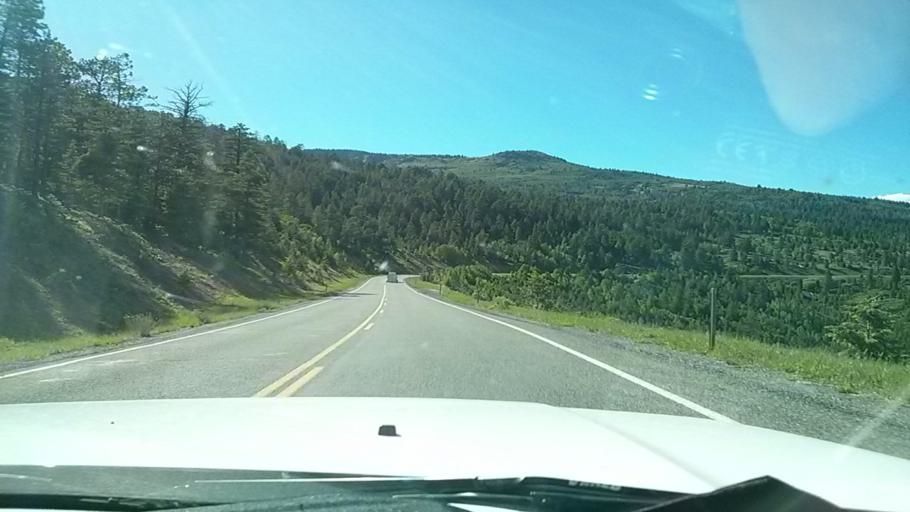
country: US
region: Utah
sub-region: Wayne County
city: Loa
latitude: 38.1196
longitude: -111.3258
